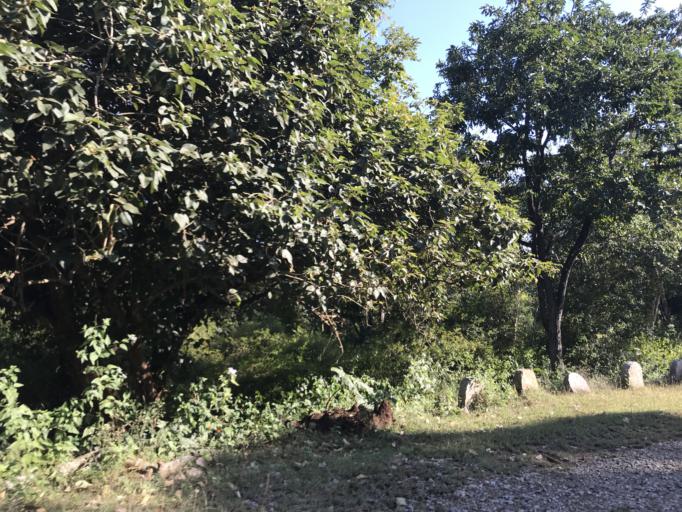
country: IN
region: Karnataka
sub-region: Mysore
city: Heggadadevankote
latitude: 11.9684
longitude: 76.2447
